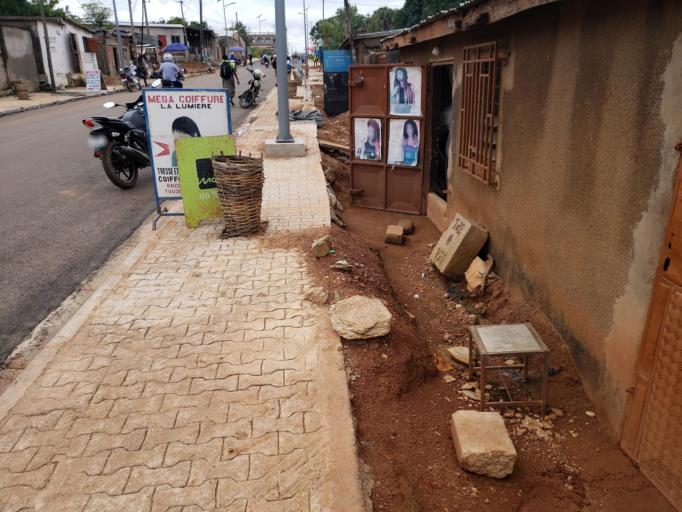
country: TG
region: Kara
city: Kara
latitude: 9.5548
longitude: 1.1947
